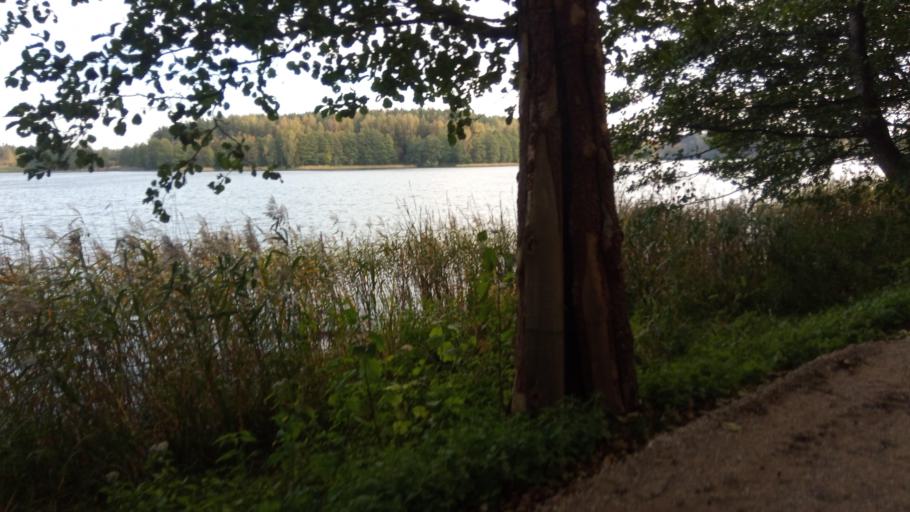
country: LT
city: Trakai
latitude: 54.6379
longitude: 24.9419
